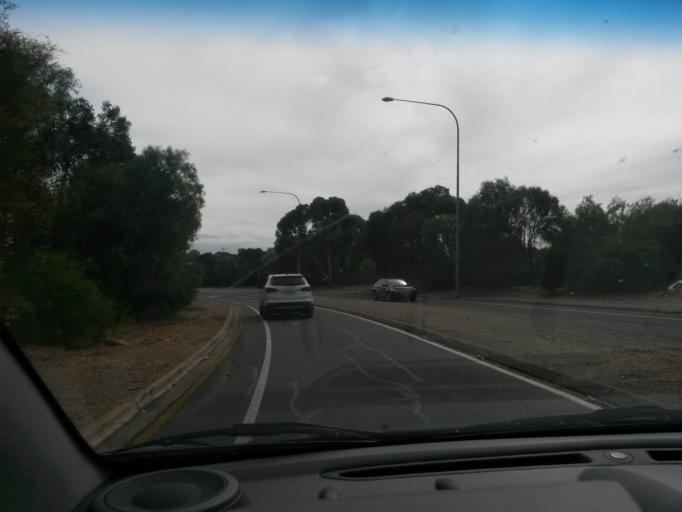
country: AU
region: South Australia
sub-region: Salisbury
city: Salisbury
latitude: -34.7693
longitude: 138.6795
